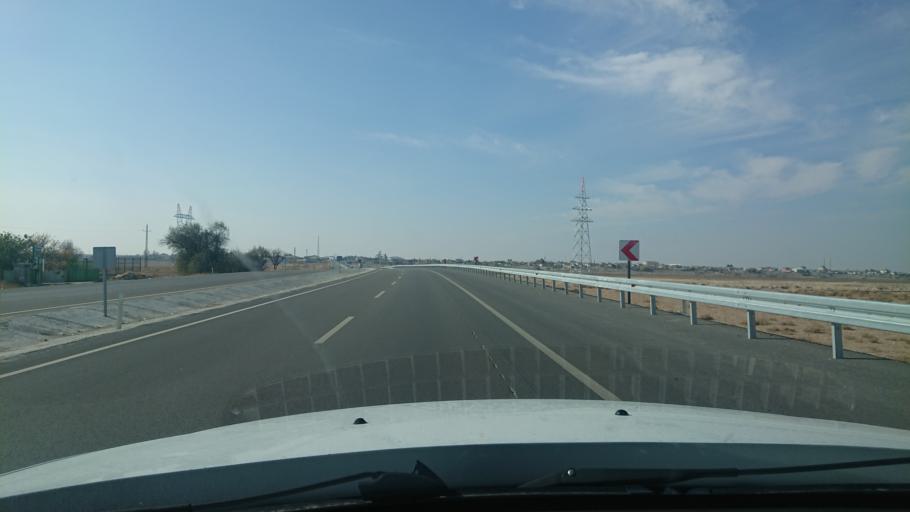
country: TR
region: Aksaray
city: Sultanhani
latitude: 38.2515
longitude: 33.4657
